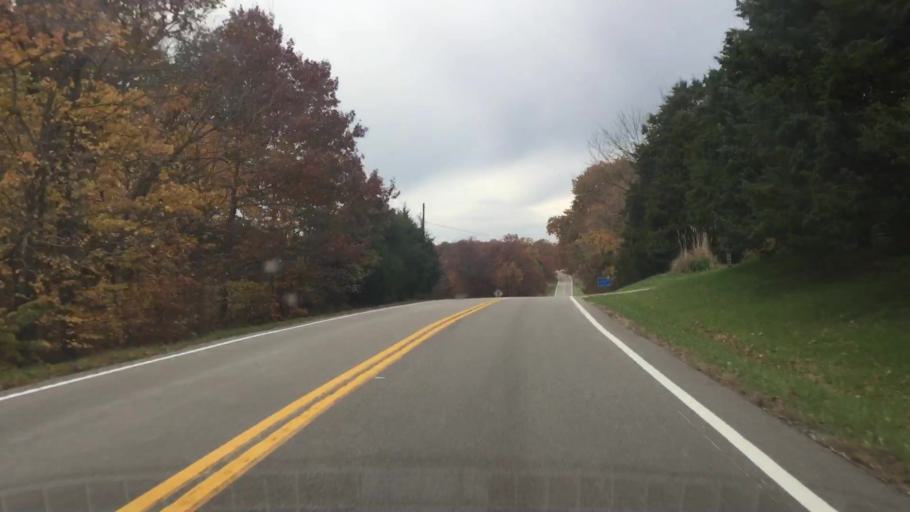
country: US
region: Missouri
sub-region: Gasconade County
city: Hermann
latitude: 38.7099
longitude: -91.6335
